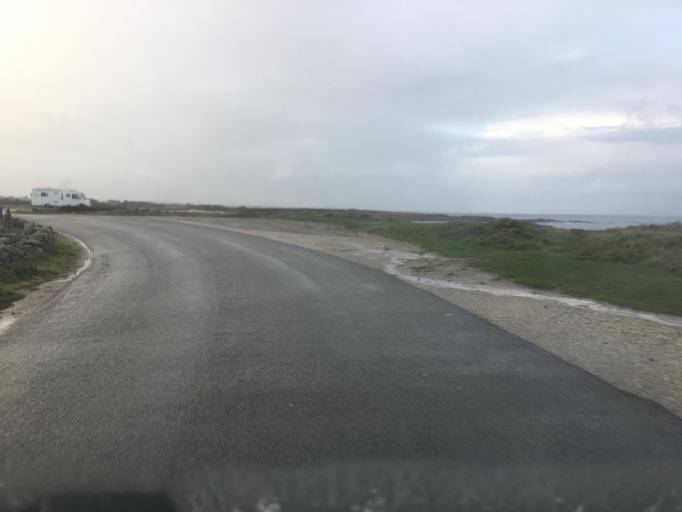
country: FR
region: Lower Normandy
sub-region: Departement de la Manche
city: Reville
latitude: 49.6951
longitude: -1.2705
